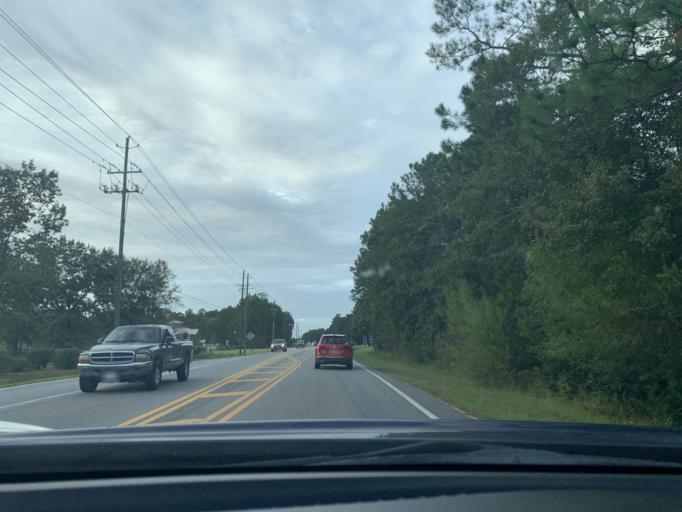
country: US
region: Georgia
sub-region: Chatham County
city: Pooler
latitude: 32.0655
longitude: -81.2735
